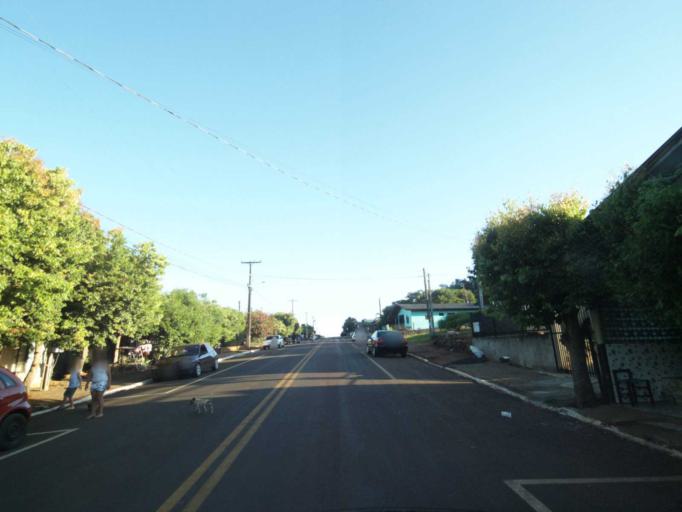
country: BR
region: Parana
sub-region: Coronel Vivida
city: Coronel Vivida
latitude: -25.9543
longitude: -52.8192
